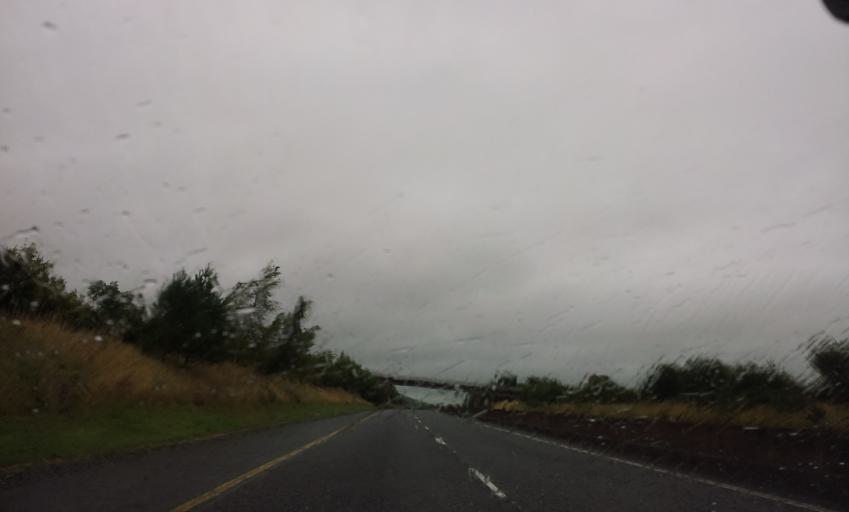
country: IE
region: Munster
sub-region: County Cork
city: Rathcormac
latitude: 52.0858
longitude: -8.2946
